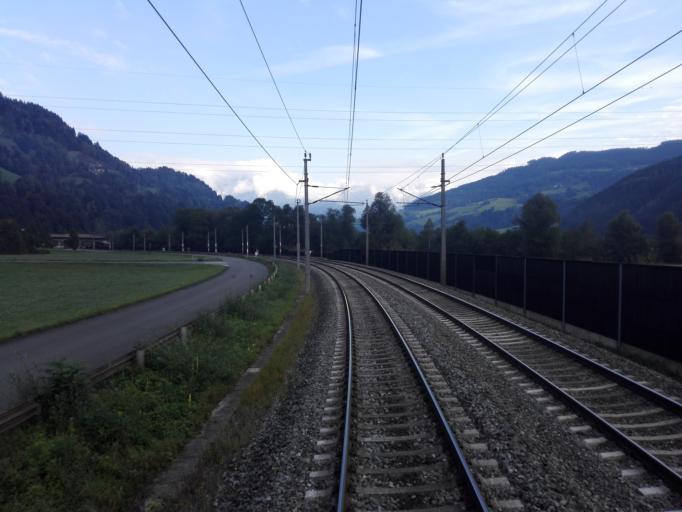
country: AT
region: Salzburg
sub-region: Politischer Bezirk Sankt Johann im Pongau
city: Sankt Johann im Pongau
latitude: 47.3791
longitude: 13.2120
